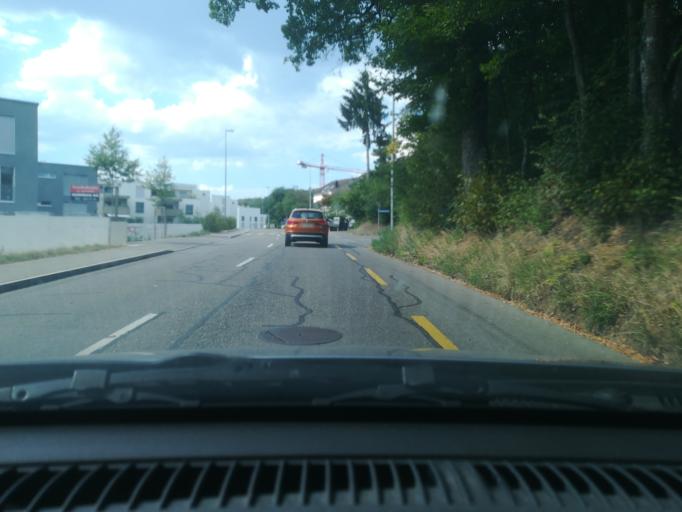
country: CH
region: Schaffhausen
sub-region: Bezirk Reiat
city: Stetten
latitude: 47.7265
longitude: 8.6640
